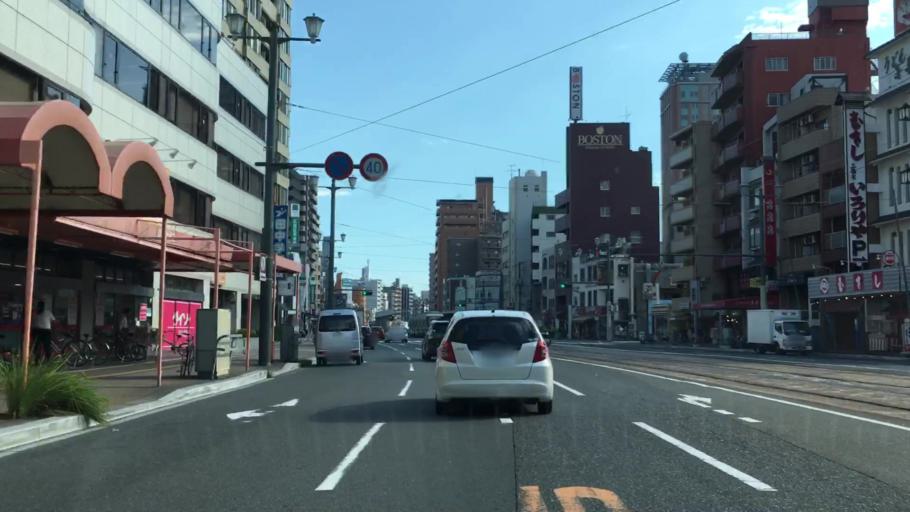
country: JP
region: Hiroshima
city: Hiroshima-shi
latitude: 34.3957
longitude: 132.4466
